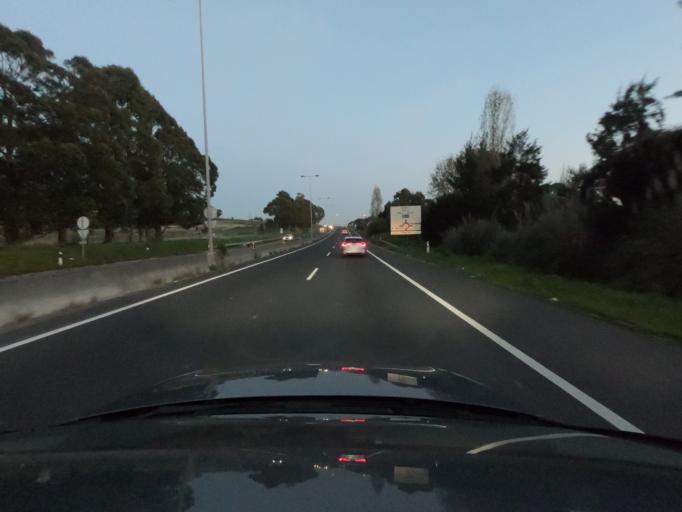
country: PT
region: Lisbon
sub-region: Sintra
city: Cacem
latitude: 38.7500
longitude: -9.3054
